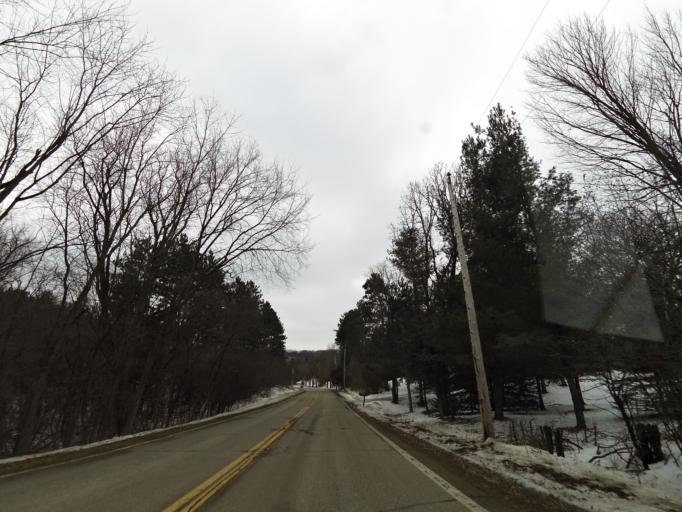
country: US
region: Minnesota
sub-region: Washington County
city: Afton
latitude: 44.9287
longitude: -92.8008
